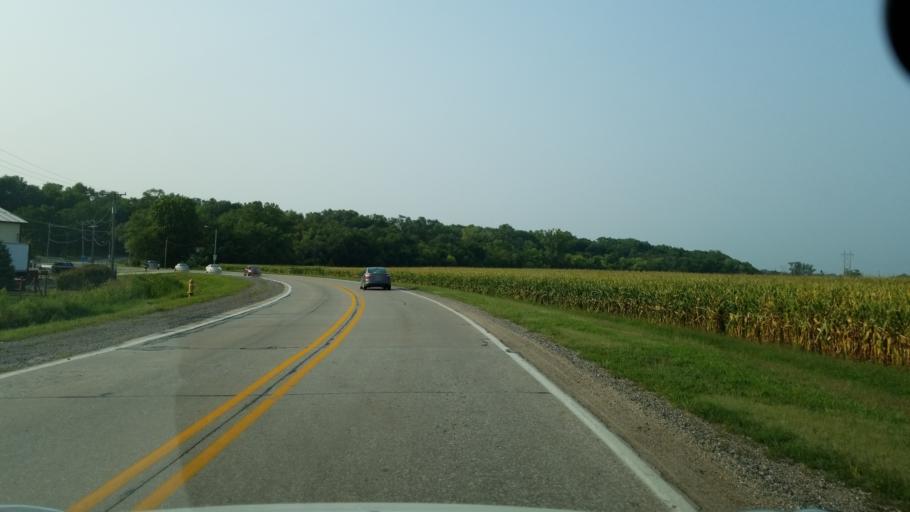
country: US
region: Nebraska
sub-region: Sarpy County
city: Bellevue
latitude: 41.1264
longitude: -95.8901
